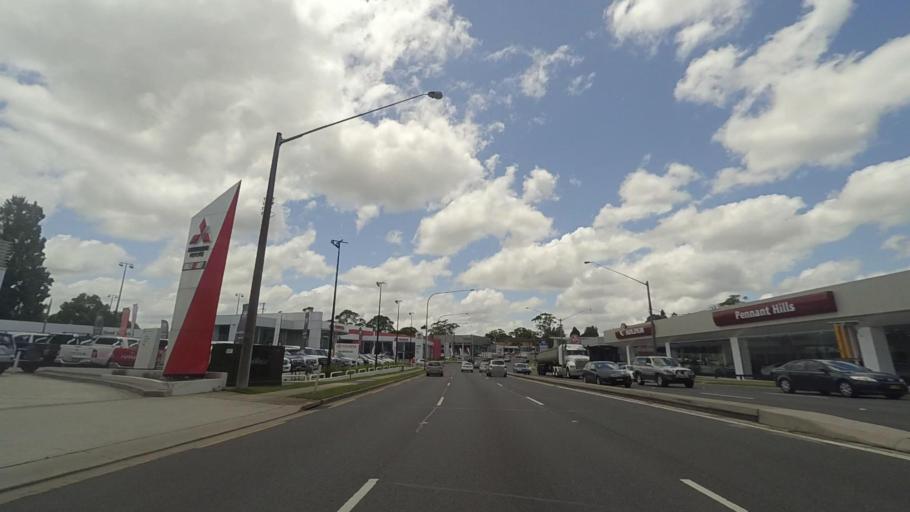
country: AU
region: New South Wales
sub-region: Hornsby Shire
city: Pennant Hills
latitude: -33.7379
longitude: 151.0740
